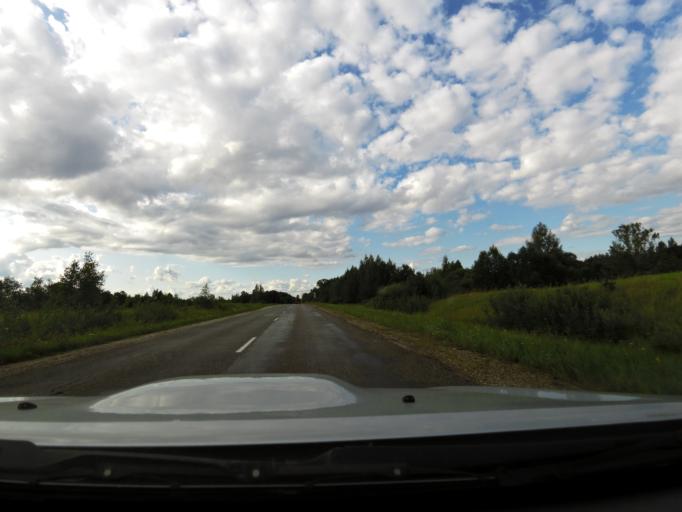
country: LV
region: Akniste
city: Akniste
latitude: 56.0208
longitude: 25.9218
